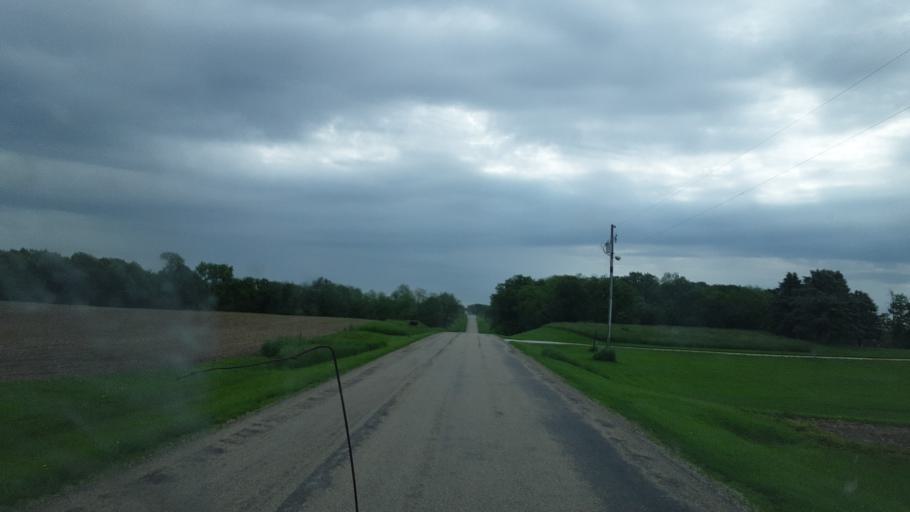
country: US
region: Illinois
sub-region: Fulton County
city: Astoria
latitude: 40.3641
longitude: -90.4558
